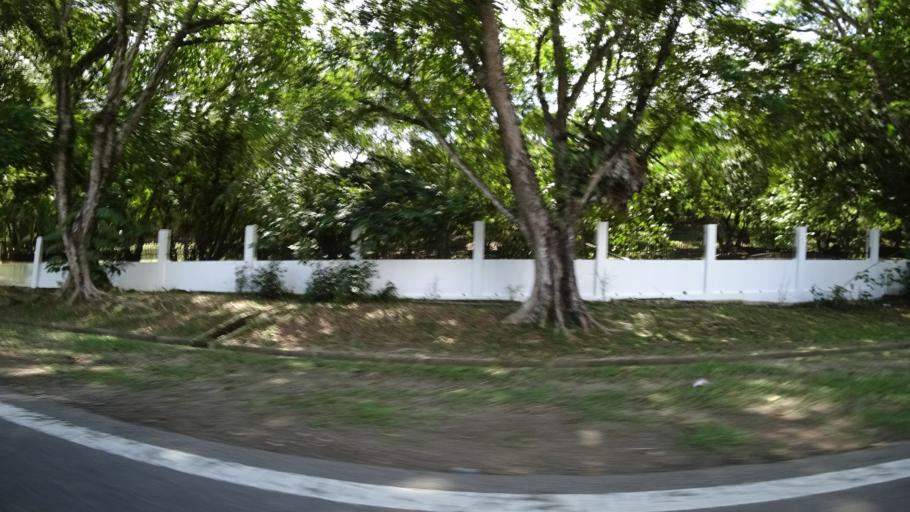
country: BN
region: Brunei and Muara
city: Bandar Seri Begawan
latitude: 4.8777
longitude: 114.9603
